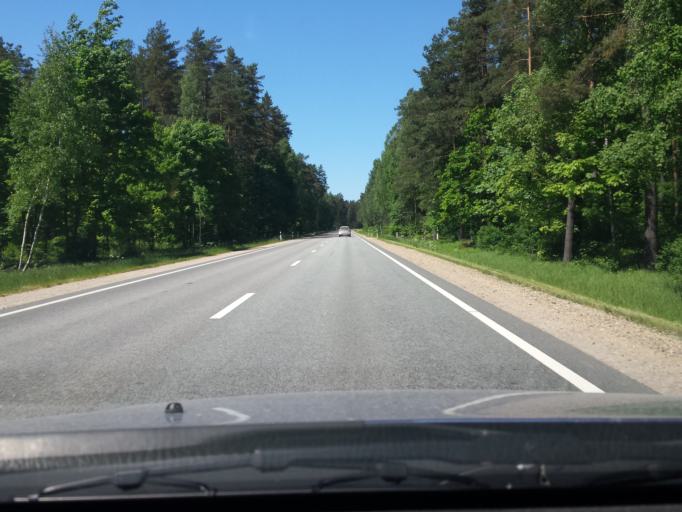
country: LV
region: Riga
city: Bergi
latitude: 56.9894
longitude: 24.3164
